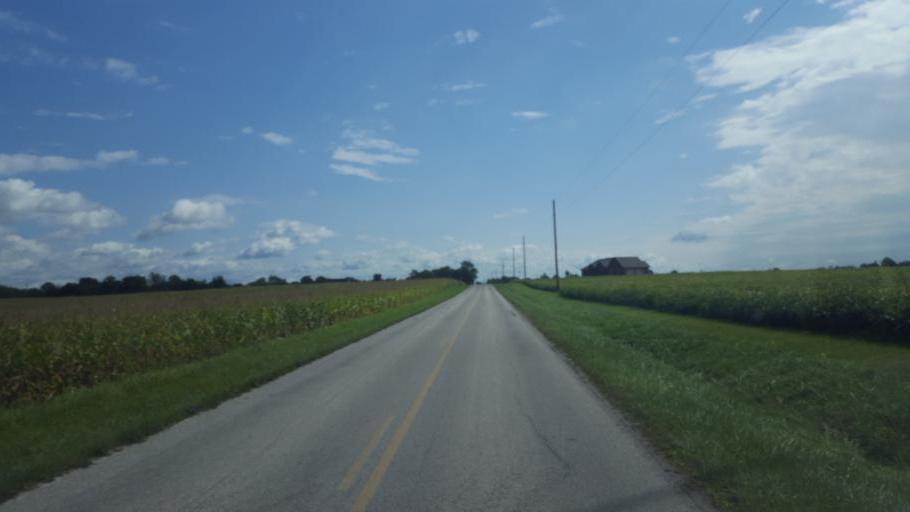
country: US
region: Ohio
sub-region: Seneca County
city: Tiffin
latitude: 41.0664
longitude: -83.0366
